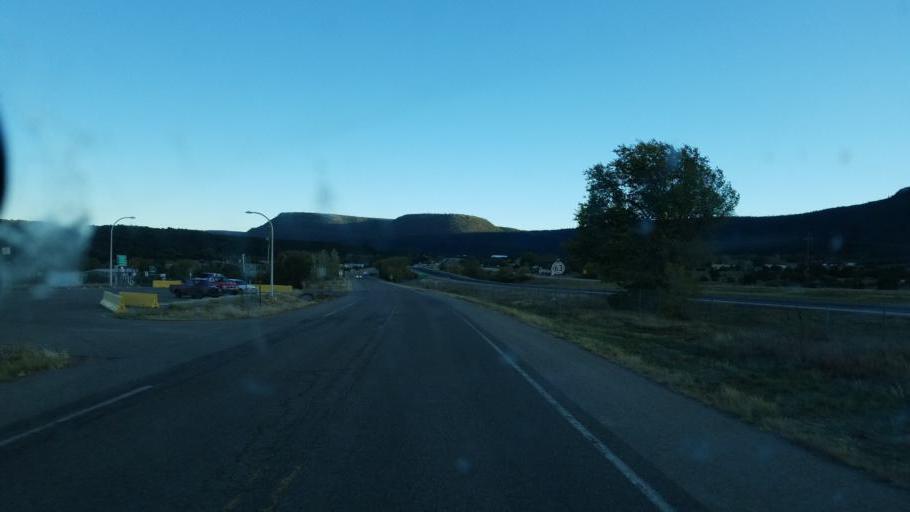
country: US
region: New Mexico
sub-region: San Miguel County
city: Pecos
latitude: 35.4994
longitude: -105.6744
